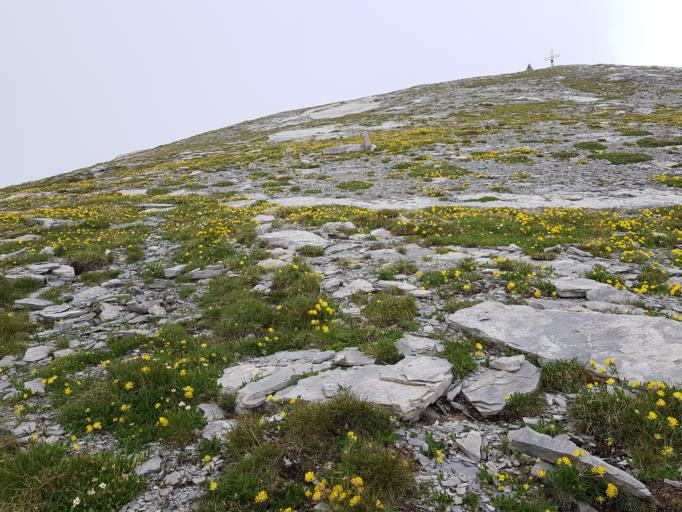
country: IT
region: Piedmont
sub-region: Provincia di Cuneo
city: Briga Alta
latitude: 44.1865
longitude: 7.7776
